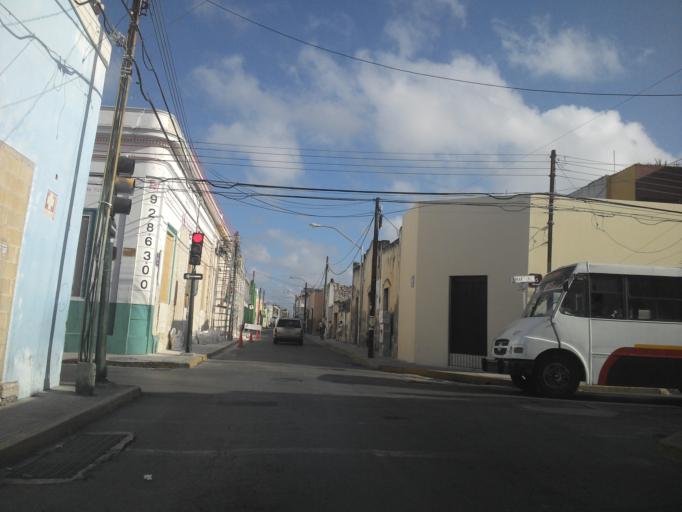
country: MX
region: Yucatan
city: Merida
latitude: 20.9662
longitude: -89.6287
